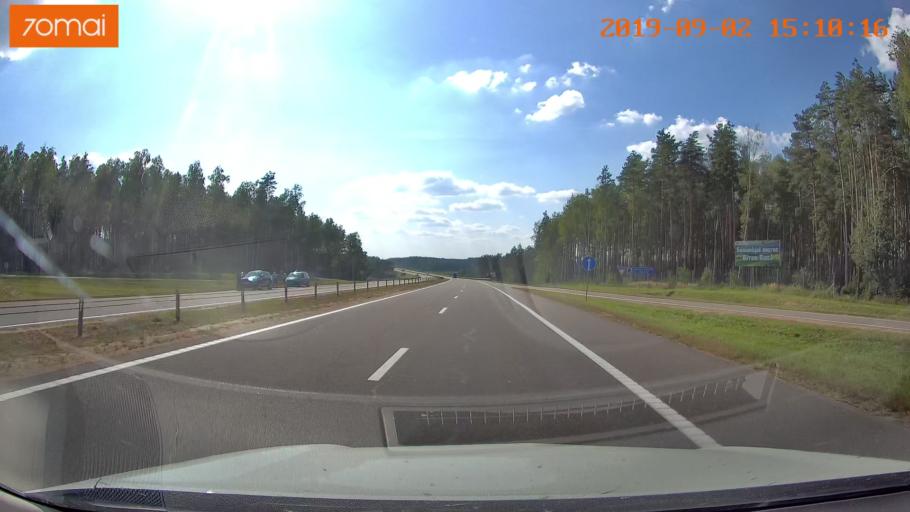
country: BY
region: Mogilev
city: Byalynichy
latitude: 53.9838
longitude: 29.7888
